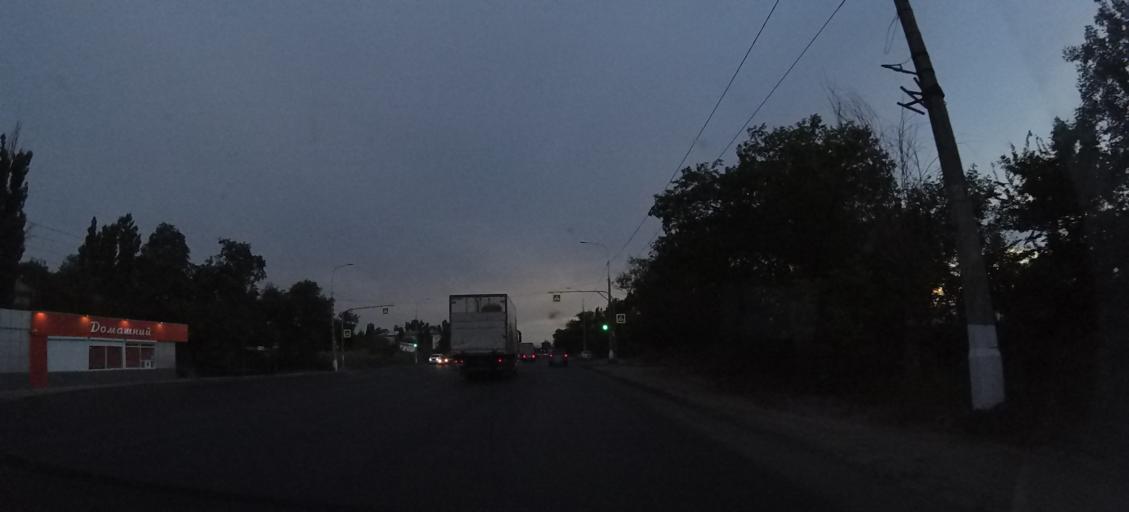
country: RU
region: Volgograd
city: Volgograd
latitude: 48.5501
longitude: 44.4494
